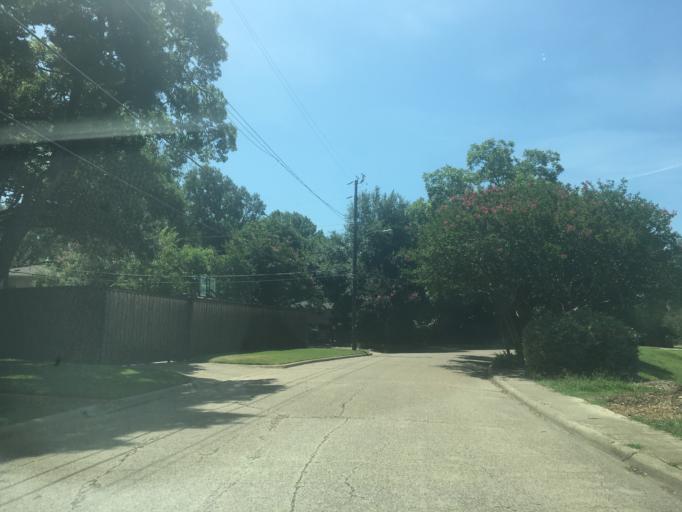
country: US
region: Texas
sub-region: Dallas County
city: University Park
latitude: 32.8714
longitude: -96.7392
